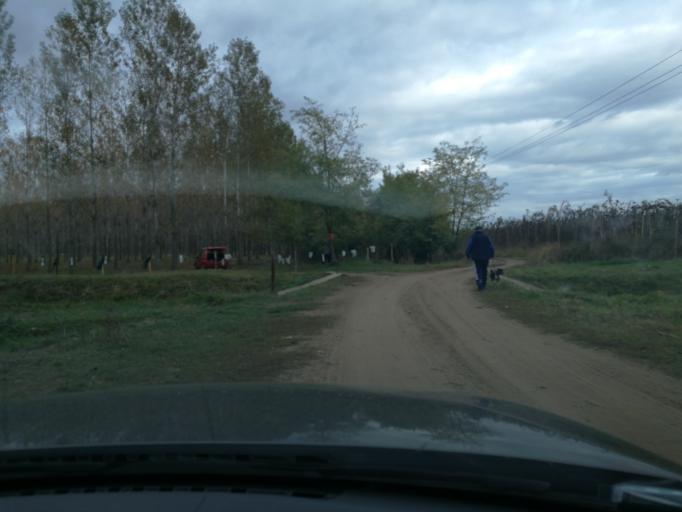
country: HU
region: Szabolcs-Szatmar-Bereg
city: Nyirpazony
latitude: 47.9973
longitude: 21.7886
